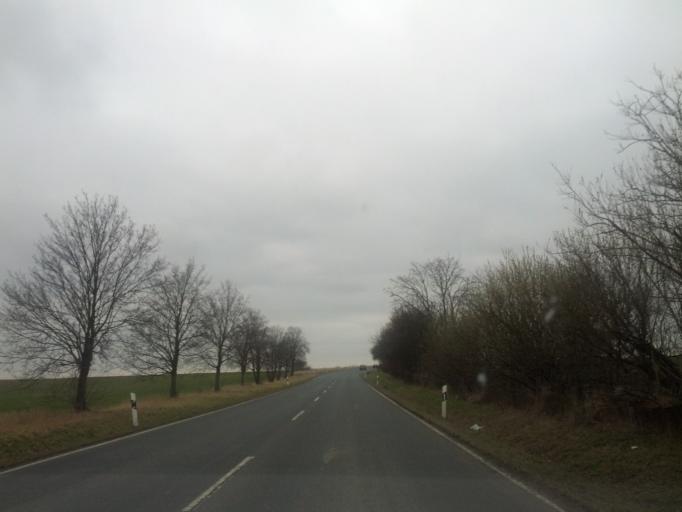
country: DE
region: Thuringia
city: Niederdorla
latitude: 51.1742
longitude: 10.4461
